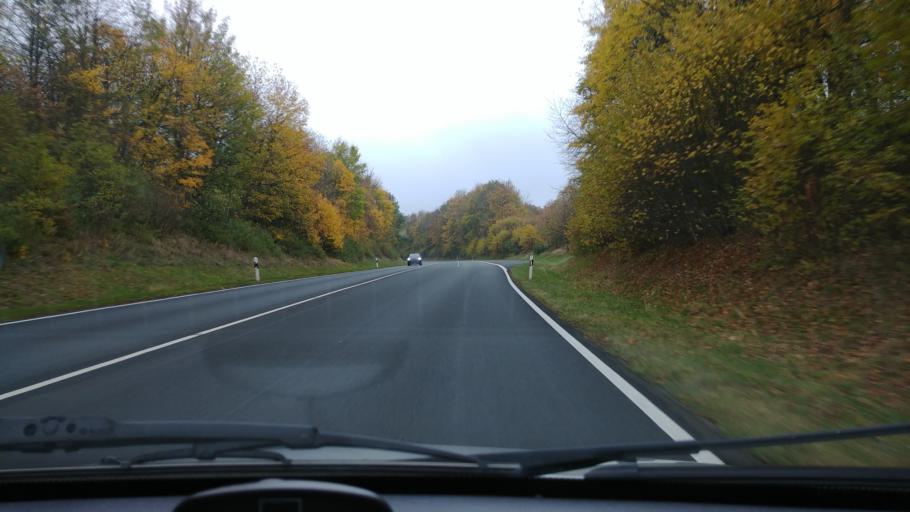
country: DE
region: Rheinland-Pfalz
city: Langenhahn
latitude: 50.5927
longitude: 7.9114
